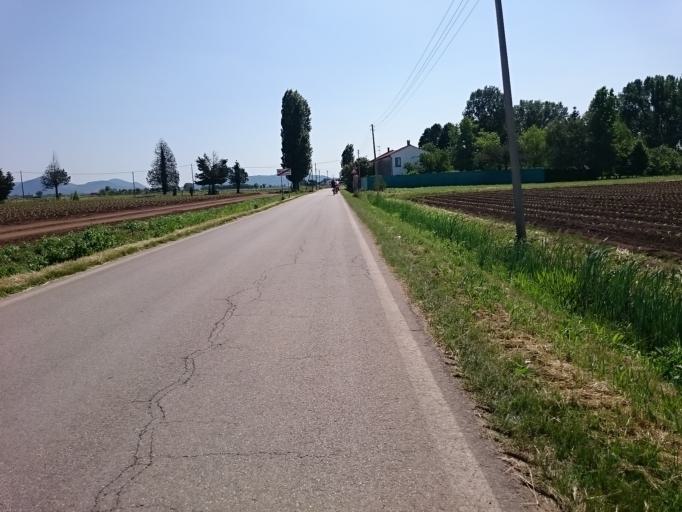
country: IT
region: Veneto
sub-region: Provincia di Padova
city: Saletto
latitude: 45.2519
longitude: 11.5501
